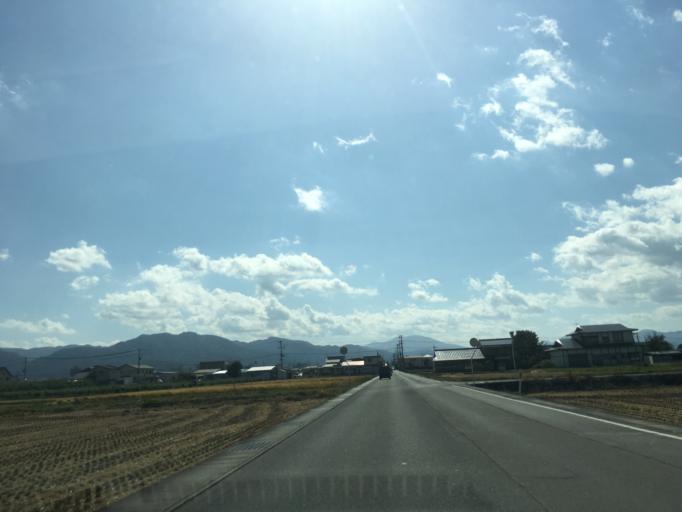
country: JP
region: Fukushima
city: Kitakata
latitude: 37.5127
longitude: 139.9199
